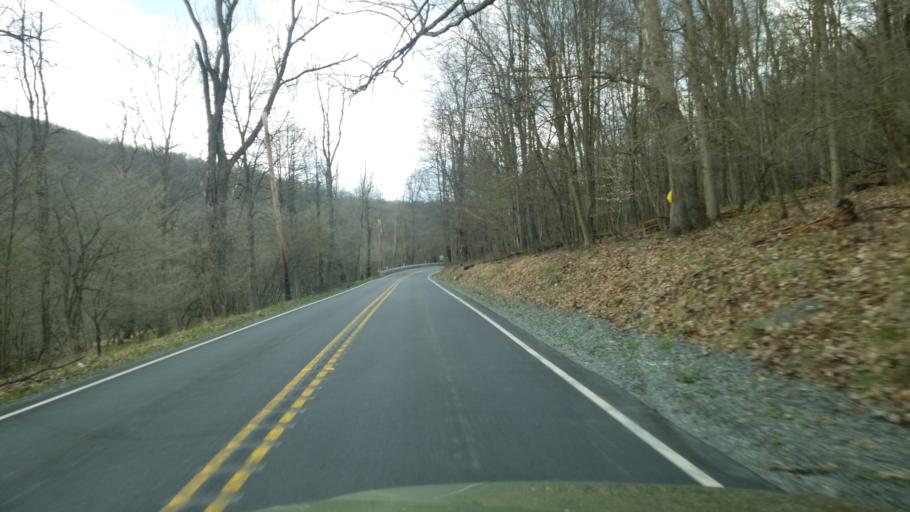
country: US
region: Pennsylvania
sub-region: Clearfield County
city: Curwensville
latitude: 40.8647
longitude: -78.4442
